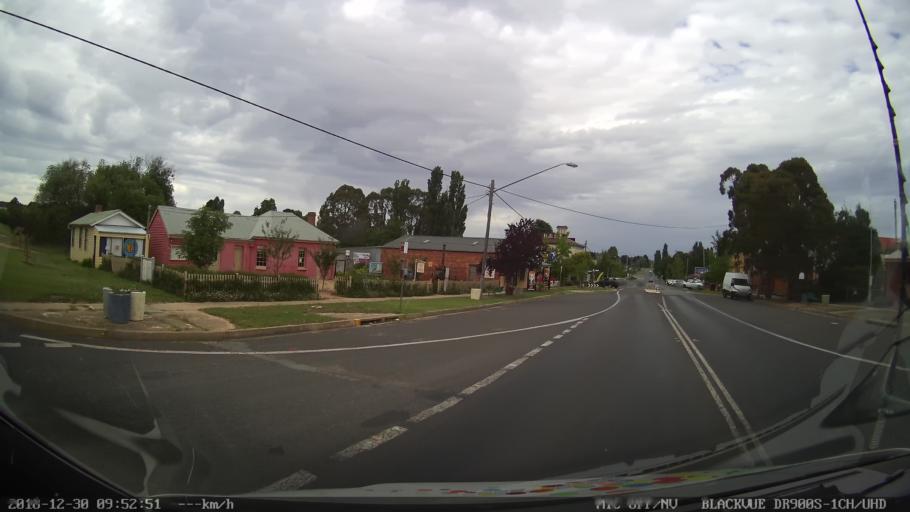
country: AU
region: New South Wales
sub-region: Cooma-Monaro
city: Cooma
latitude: -36.5122
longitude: 149.2843
